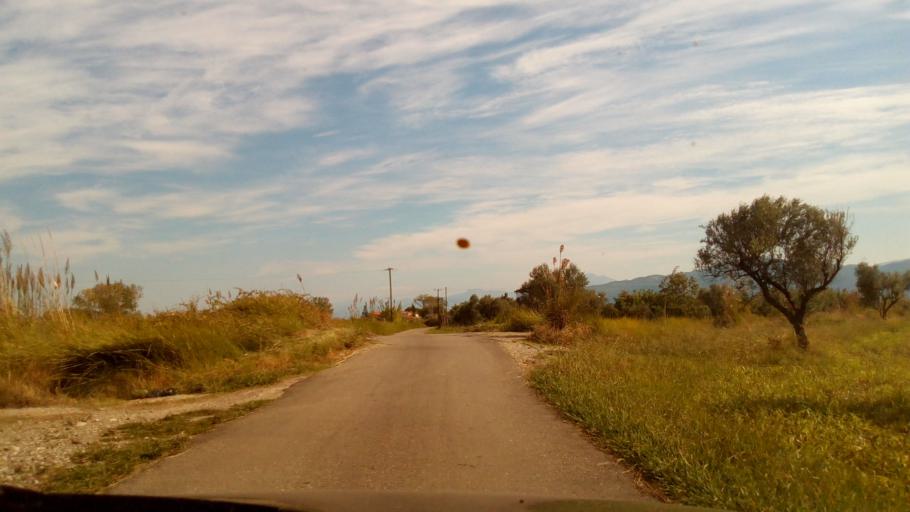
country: GR
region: West Greece
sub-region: Nomos Aitolias kai Akarnanias
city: Nafpaktos
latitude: 38.3928
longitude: 21.9101
